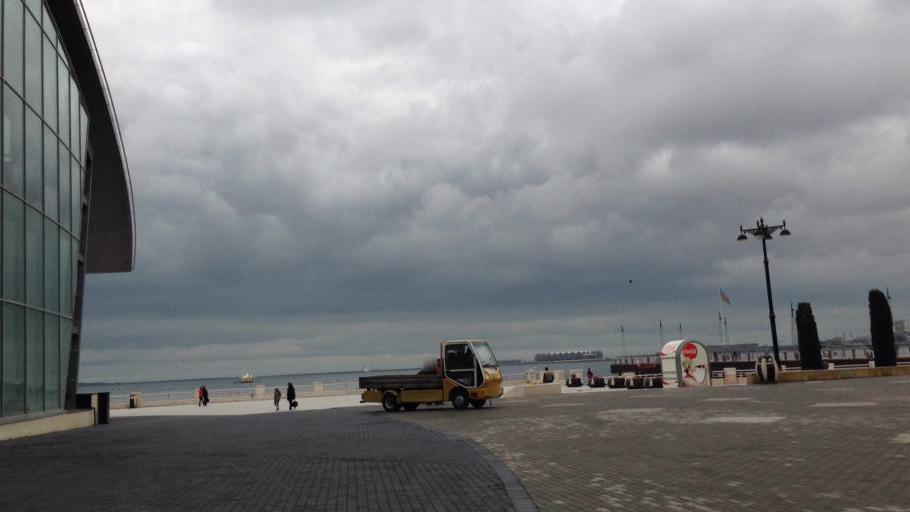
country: AZ
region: Baki
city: Baku
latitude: 40.3693
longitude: 49.8442
